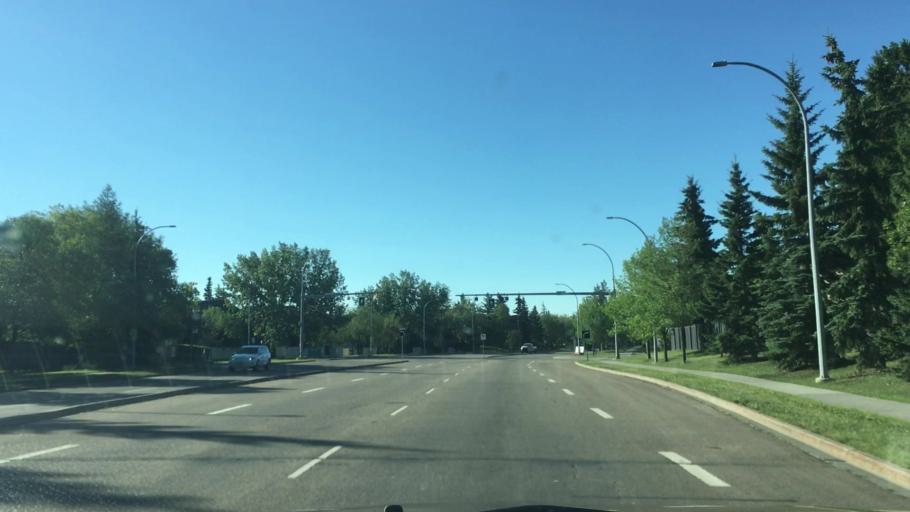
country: CA
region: Alberta
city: Edmonton
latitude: 53.4570
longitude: -113.5356
